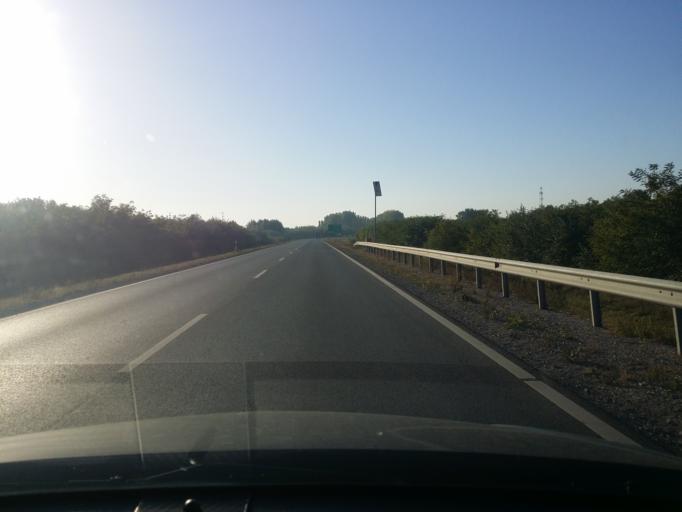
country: HU
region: Bacs-Kiskun
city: Kecskemet
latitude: 46.9128
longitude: 19.7349
